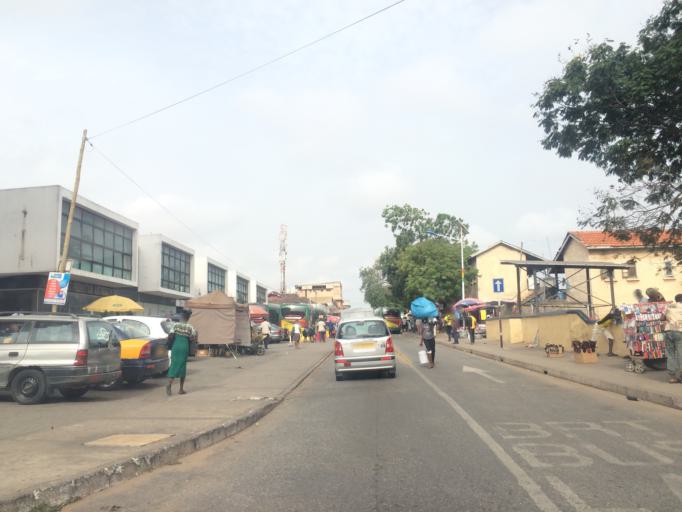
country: GH
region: Greater Accra
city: Accra
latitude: 5.5516
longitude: -0.2107
